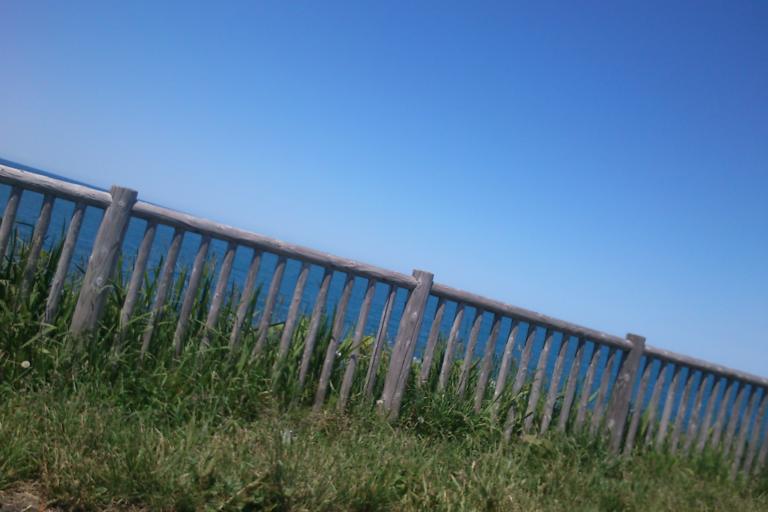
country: JP
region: Hokkaido
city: Rumoi
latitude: 43.8797
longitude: 141.5866
